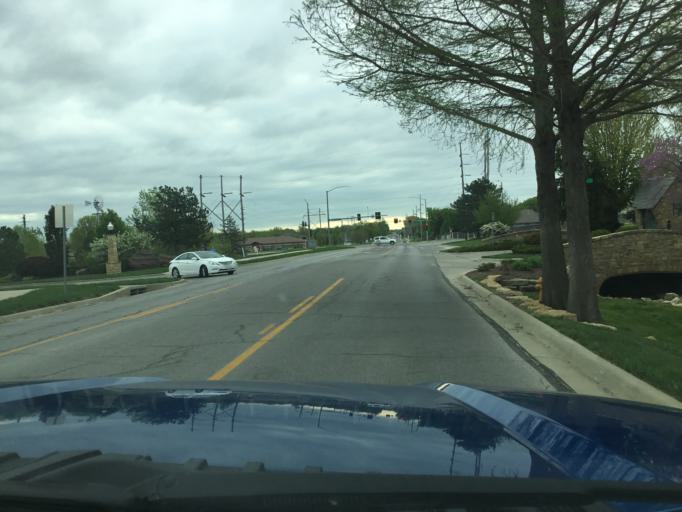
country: US
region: Kansas
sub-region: Douglas County
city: Lawrence
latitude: 38.9861
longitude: -95.2807
